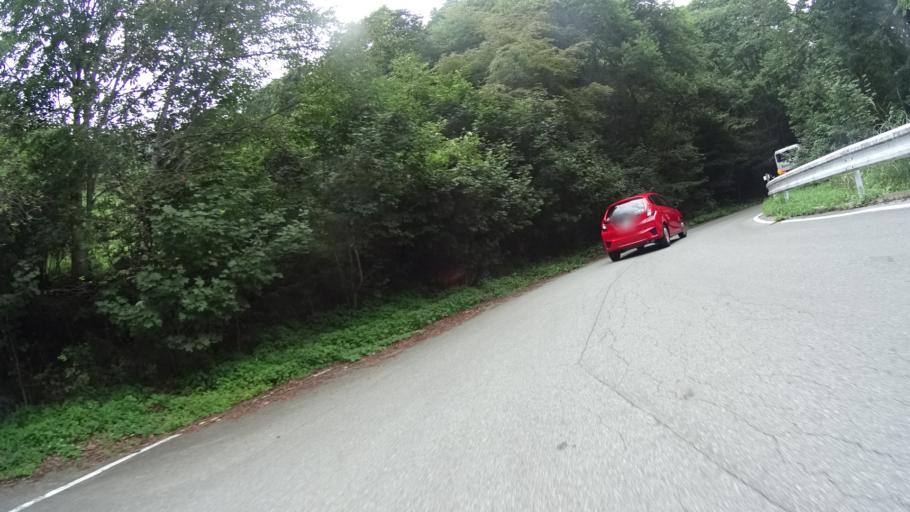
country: JP
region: Yamanashi
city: Enzan
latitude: 35.7984
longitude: 138.6835
